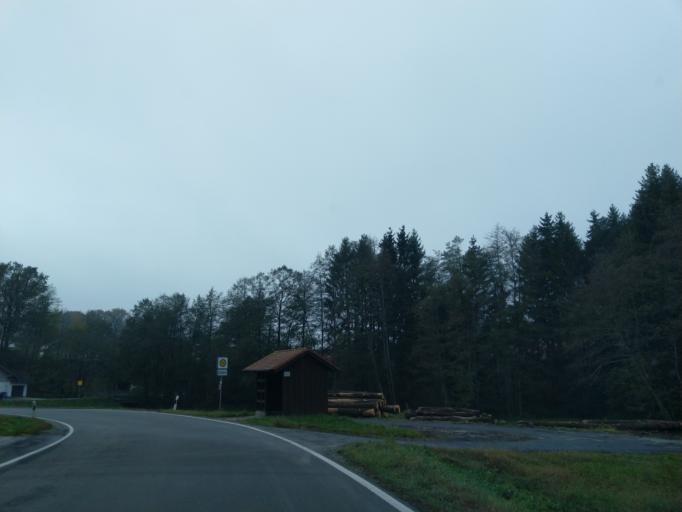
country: DE
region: Bavaria
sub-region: Lower Bavaria
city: Schollnach
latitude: 48.7734
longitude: 13.1762
